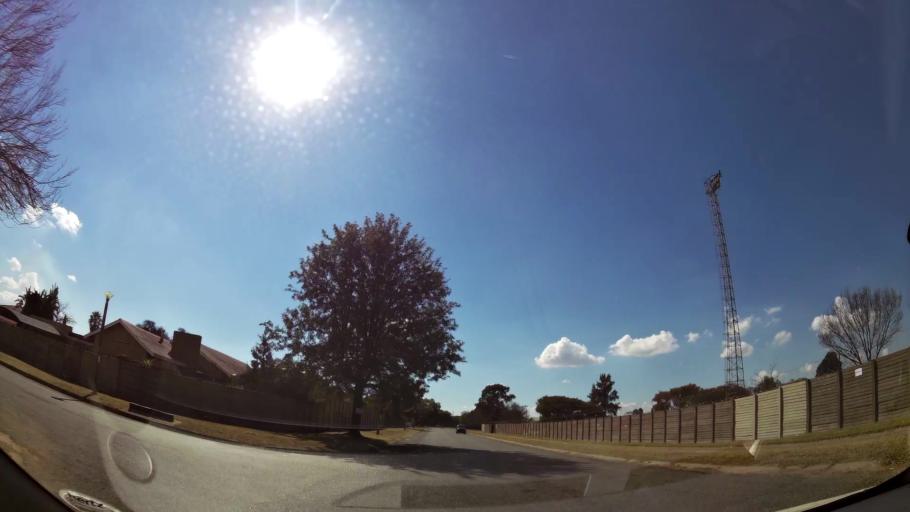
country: ZA
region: Mpumalanga
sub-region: Nkangala District Municipality
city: Witbank
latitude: -25.8843
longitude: 29.2252
